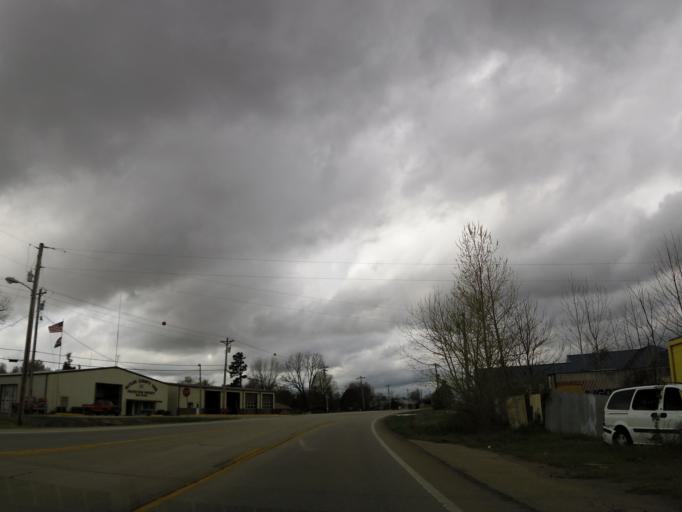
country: US
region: Missouri
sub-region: Butler County
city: Poplar Bluff
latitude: 36.7342
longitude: -90.4308
